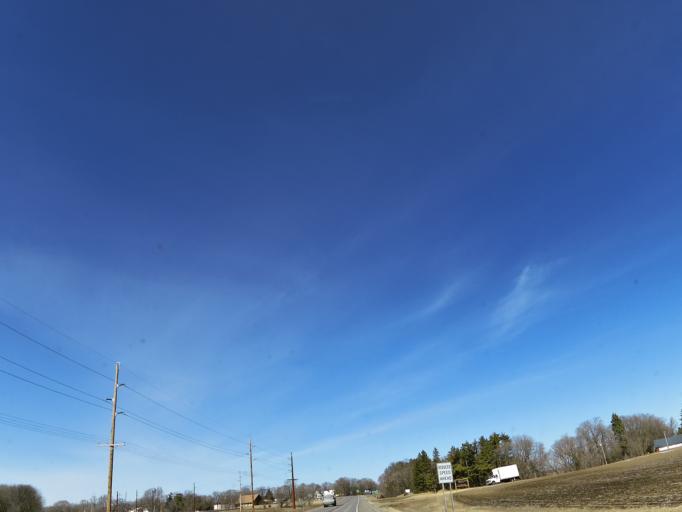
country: US
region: Minnesota
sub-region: Wright County
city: Annandale
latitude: 45.2892
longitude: -94.2075
